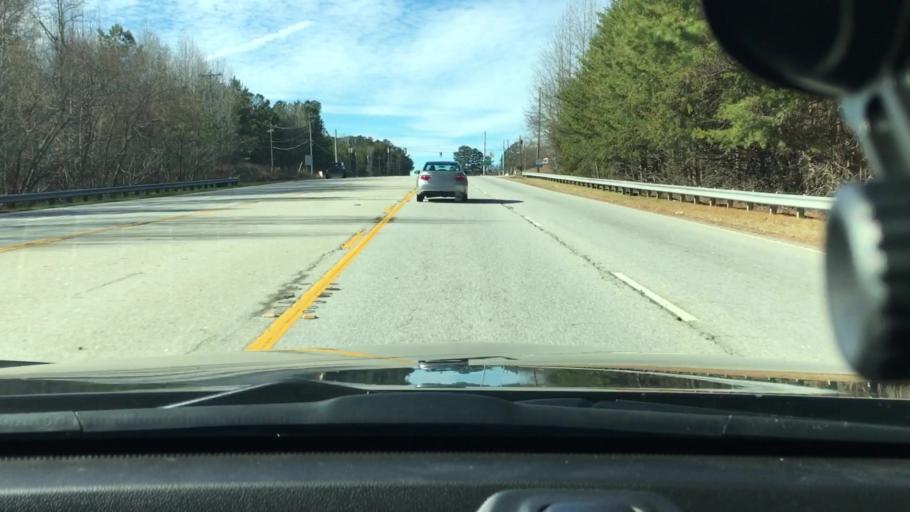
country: US
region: South Carolina
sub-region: Spartanburg County
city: Pacolet
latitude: 34.9253
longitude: -81.8351
